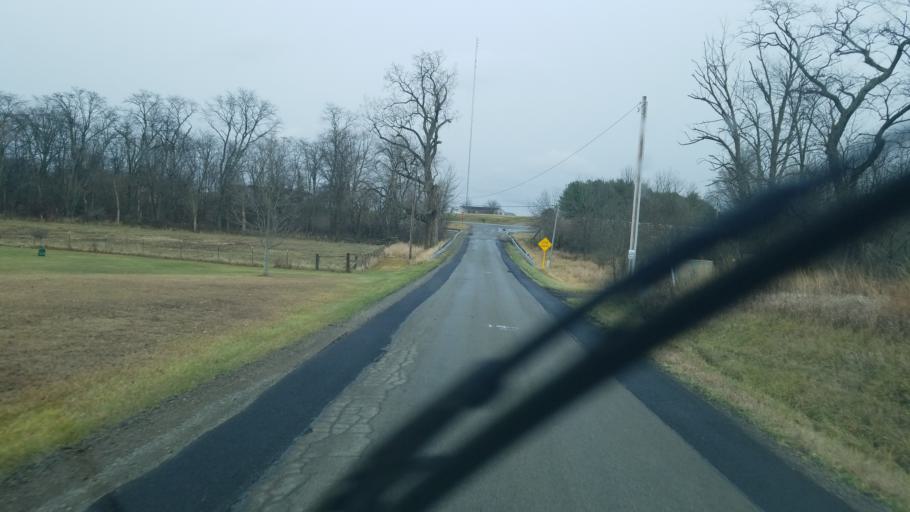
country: US
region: Ohio
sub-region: Union County
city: Marysville
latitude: 40.3064
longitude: -83.3351
